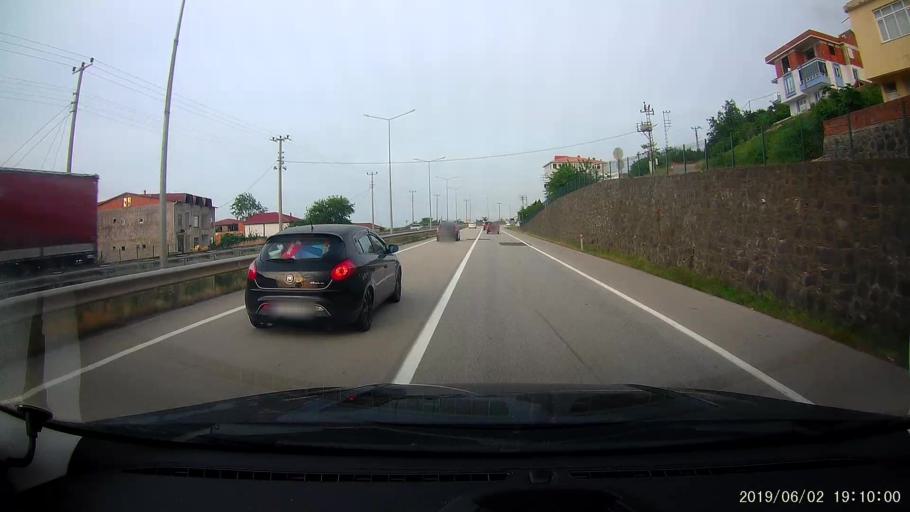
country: TR
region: Ordu
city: Gulyali
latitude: 40.9717
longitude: 38.0377
